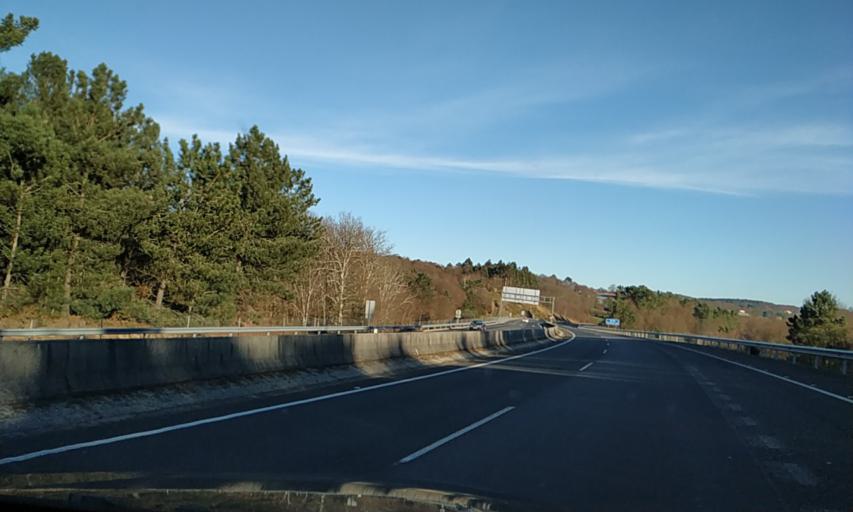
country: ES
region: Galicia
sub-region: Provincia de Pontevedra
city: Lalin
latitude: 42.6717
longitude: -8.1573
